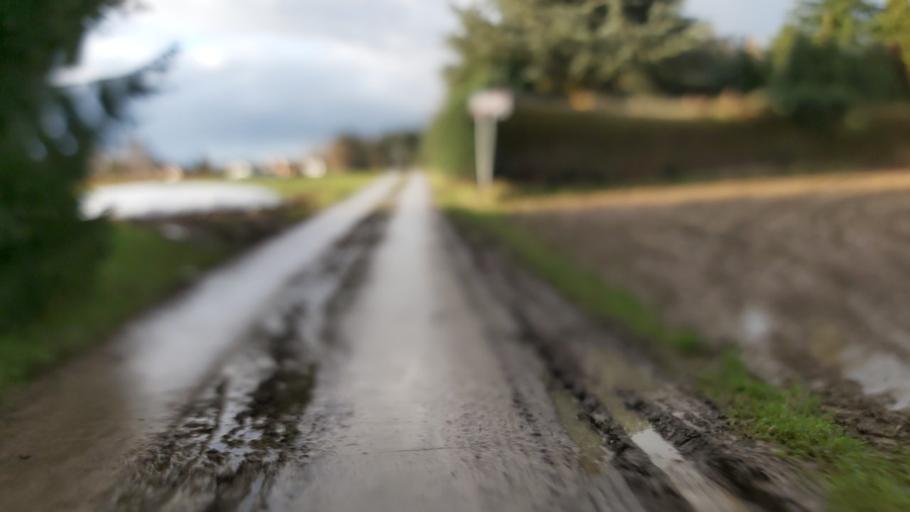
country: BE
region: Flanders
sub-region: Provincie Vlaams-Brabant
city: Tienen
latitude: 50.8248
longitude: 4.9288
